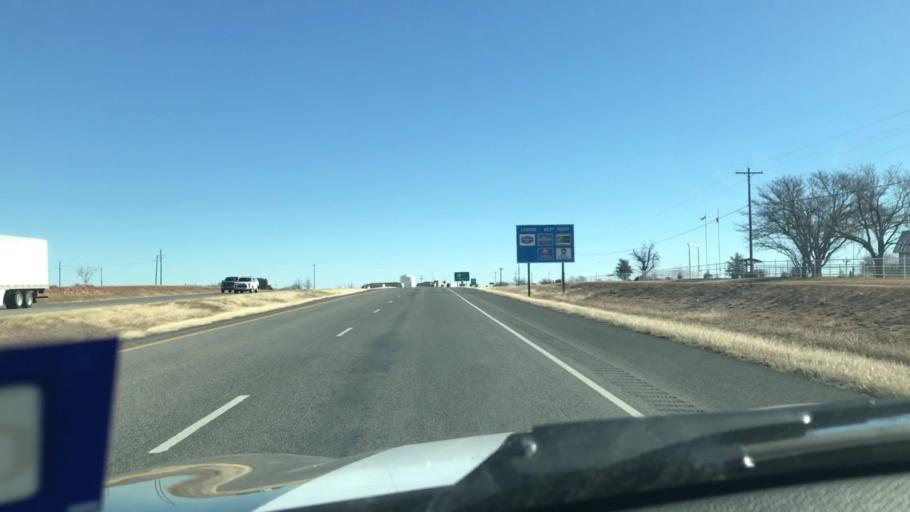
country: US
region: Texas
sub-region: Scurry County
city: Snyder
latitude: 32.7129
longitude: -100.8753
